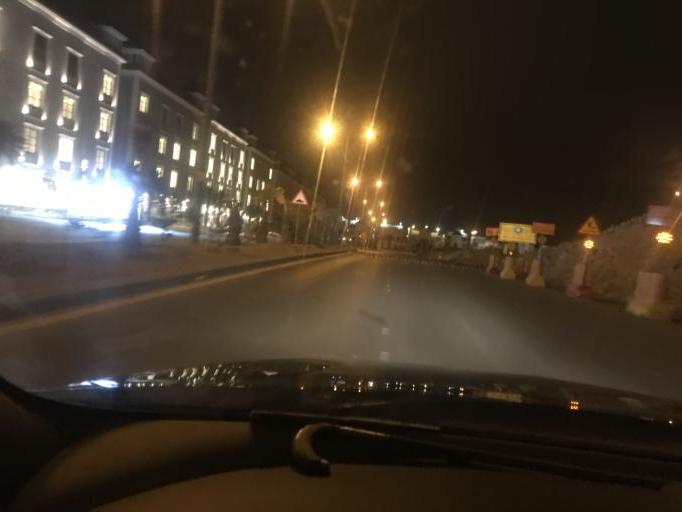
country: SA
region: Ar Riyad
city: Riyadh
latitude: 24.8041
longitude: 46.6827
